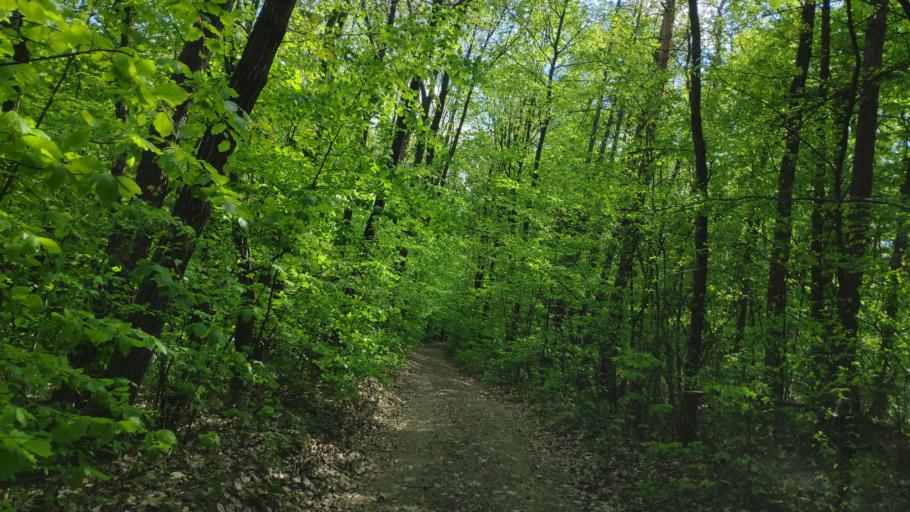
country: SK
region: Kosicky
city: Kosice
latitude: 48.6745
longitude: 21.4337
